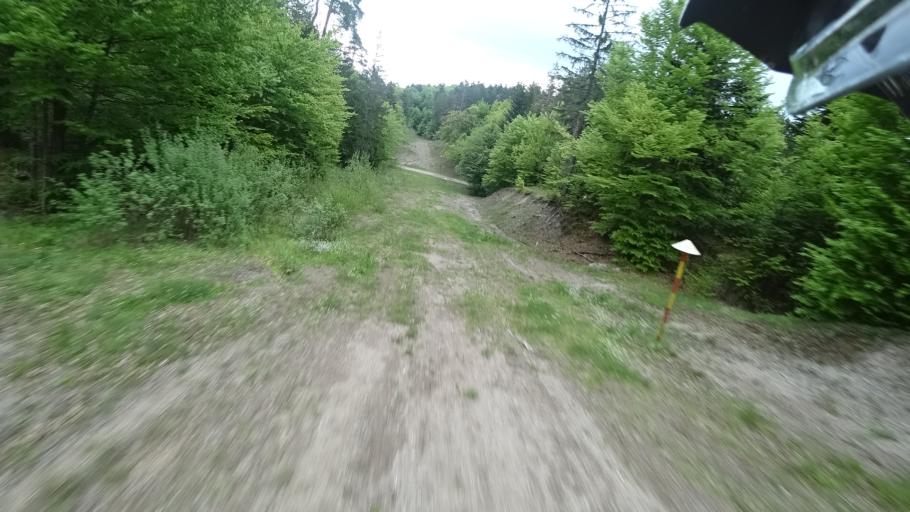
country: HR
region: Licko-Senjska
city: Jezerce
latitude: 44.8813
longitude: 15.4318
